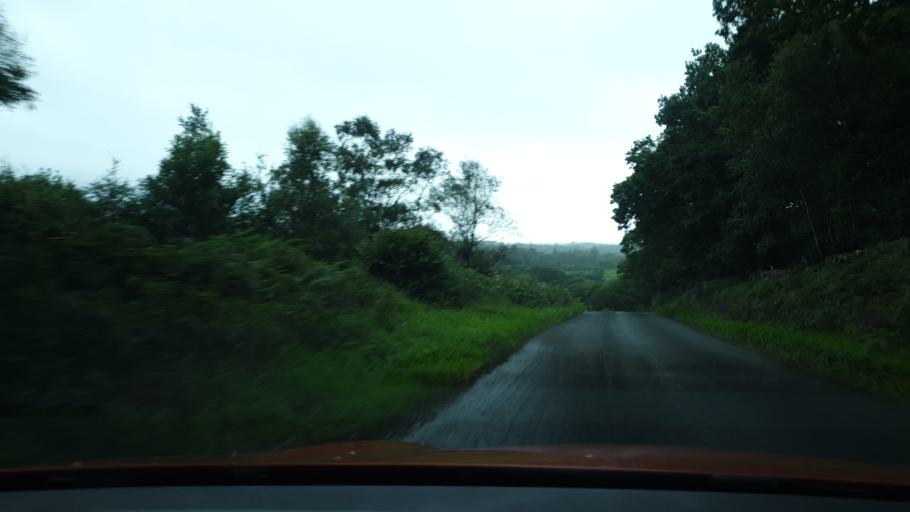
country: GB
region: England
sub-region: Cumbria
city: Seascale
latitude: 54.4080
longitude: -3.3669
